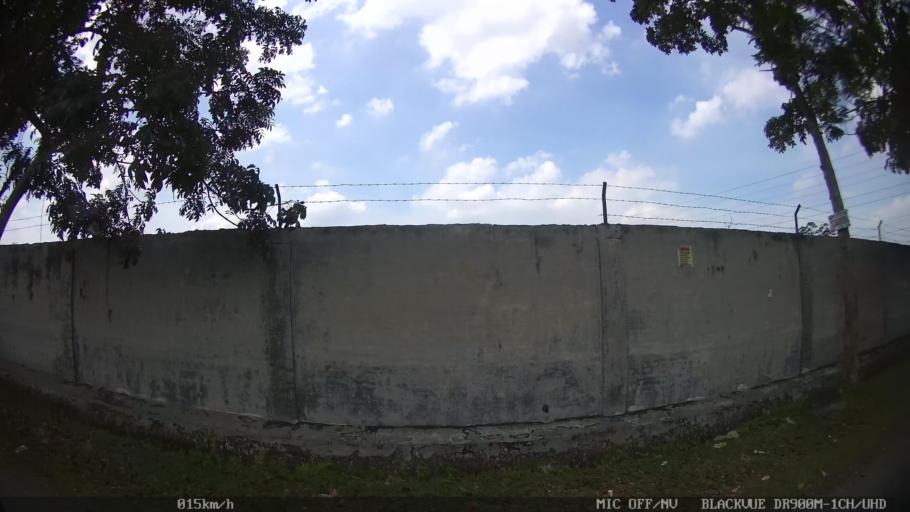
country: ID
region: North Sumatra
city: Binjai
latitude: 3.6209
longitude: 98.5181
